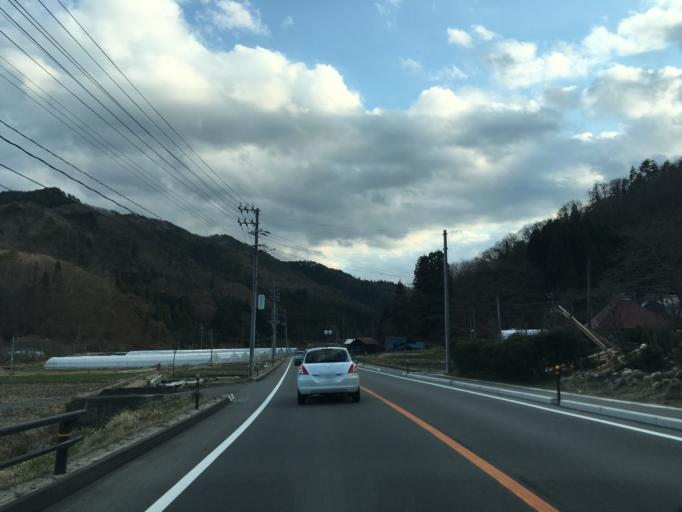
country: JP
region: Fukushima
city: Ishikawa
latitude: 37.0927
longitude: 140.5288
